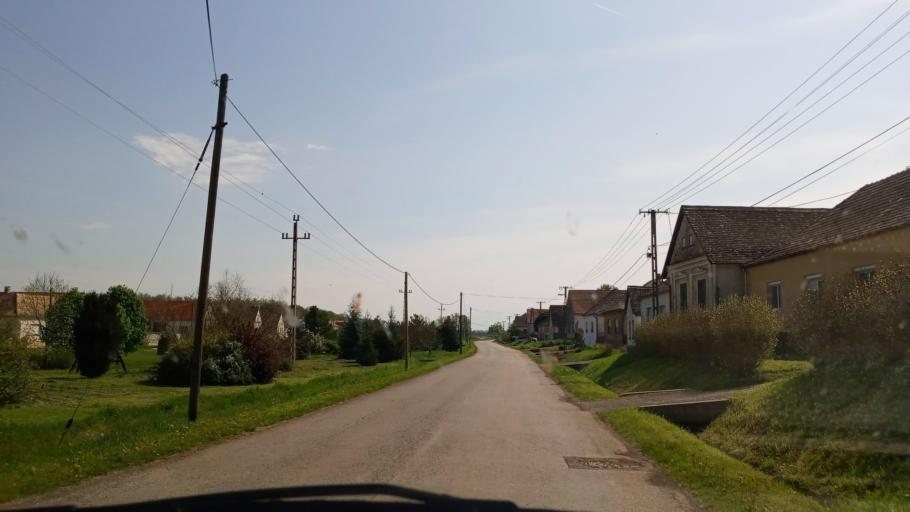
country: HU
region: Baranya
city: Boly
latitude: 45.9464
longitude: 18.5802
